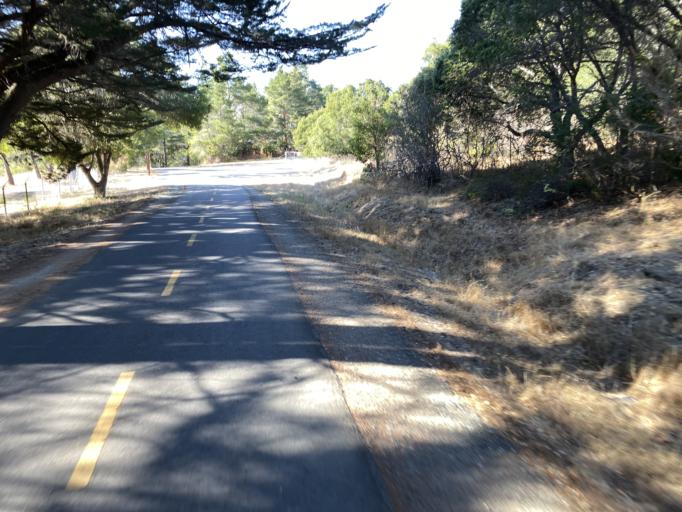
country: US
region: California
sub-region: San Mateo County
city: Hillsborough
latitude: 37.5575
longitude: -122.3906
